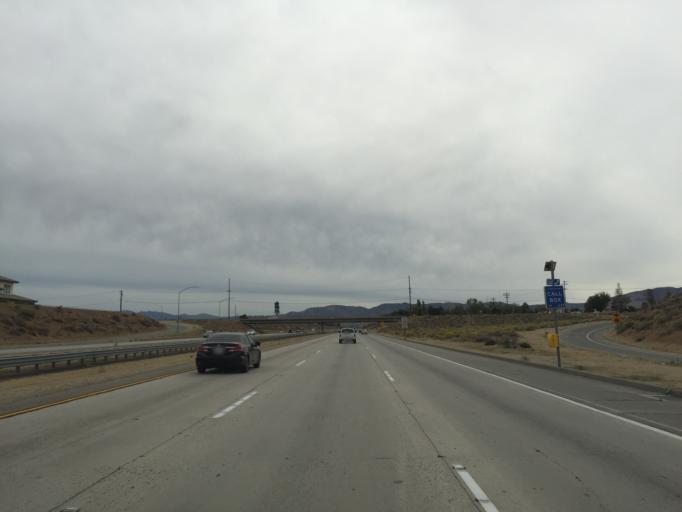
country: US
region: California
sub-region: Los Angeles County
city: Desert View Highlands
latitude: 34.6340
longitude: -118.1534
